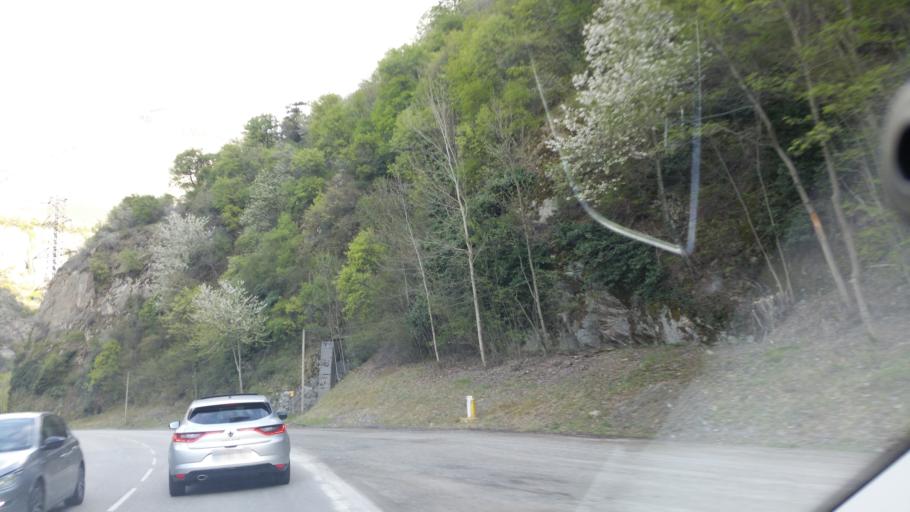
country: FR
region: Rhone-Alpes
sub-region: Departement de la Savoie
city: Saint-Jean-de-Maurienne
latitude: 45.3150
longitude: 6.3262
